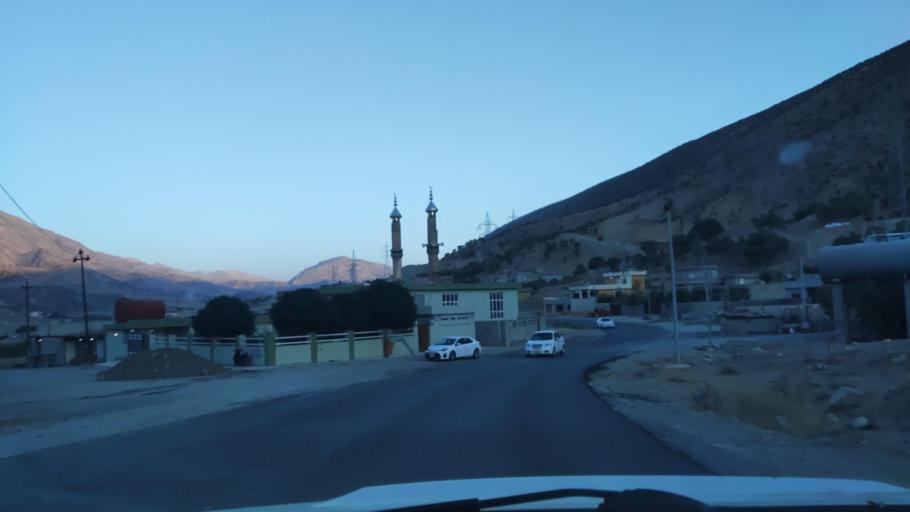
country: IQ
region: Arbil
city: Ruwandiz
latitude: 36.5923
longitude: 44.3856
